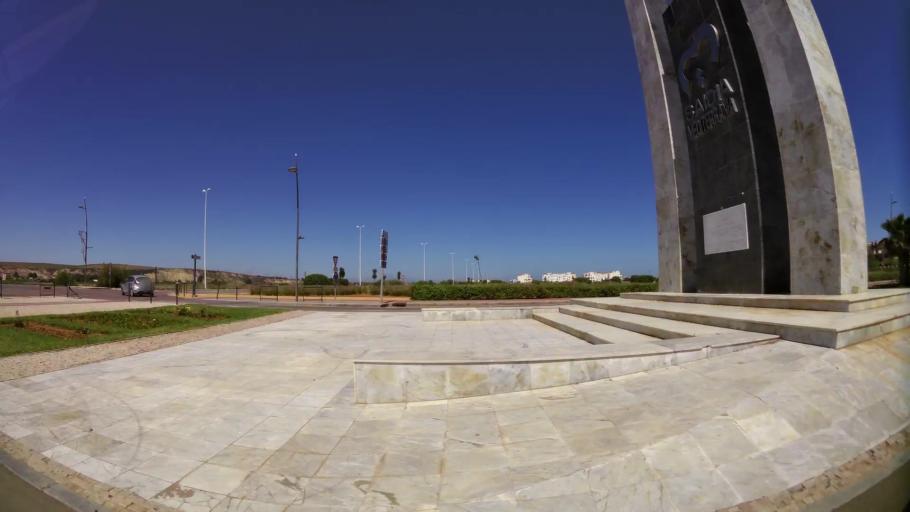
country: MA
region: Oriental
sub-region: Berkane-Taourirt
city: Madagh
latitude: 35.0972
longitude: -2.3011
